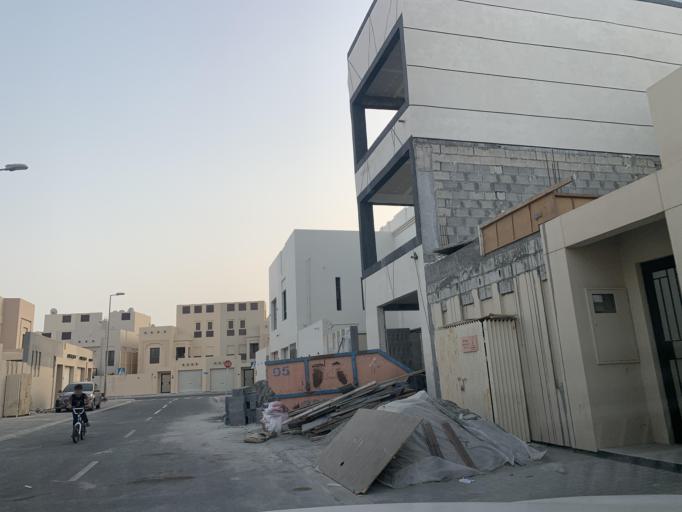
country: BH
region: Manama
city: Jidd Hafs
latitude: 26.2238
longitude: 50.4458
